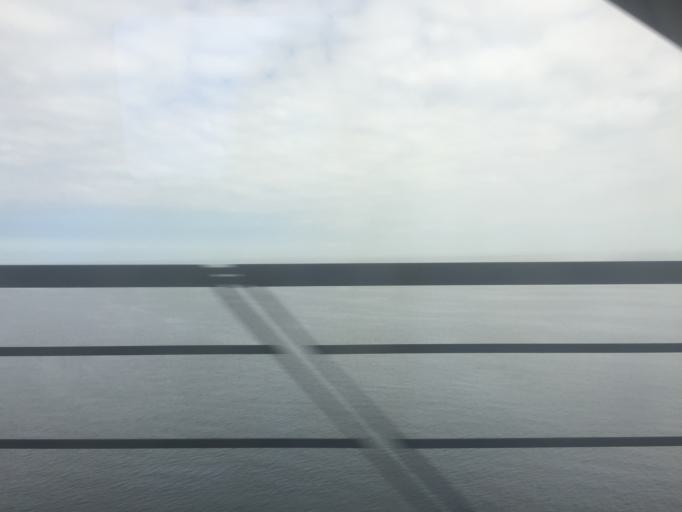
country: SE
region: Skane
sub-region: Malmo
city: Bunkeflostrand
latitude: 55.5670
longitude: 12.8772
